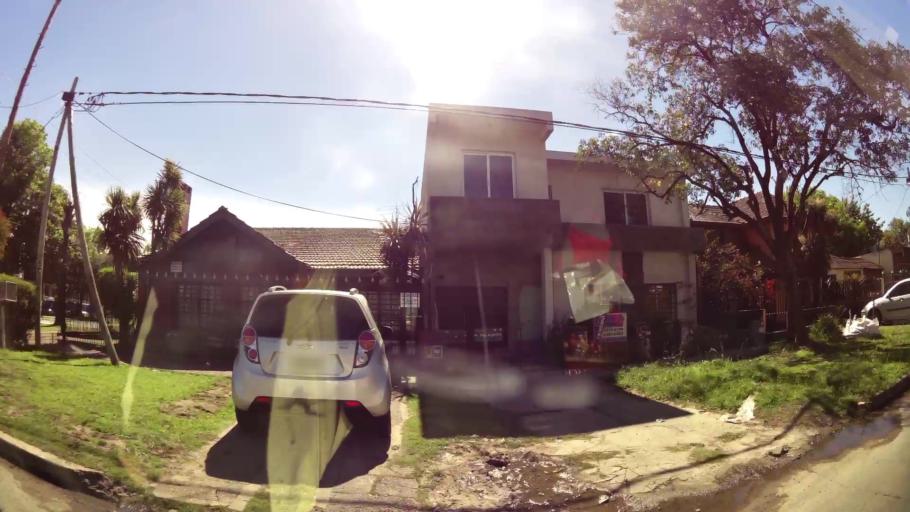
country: AR
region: Buenos Aires
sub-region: Partido de Almirante Brown
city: Adrogue
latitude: -34.7953
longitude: -58.3639
